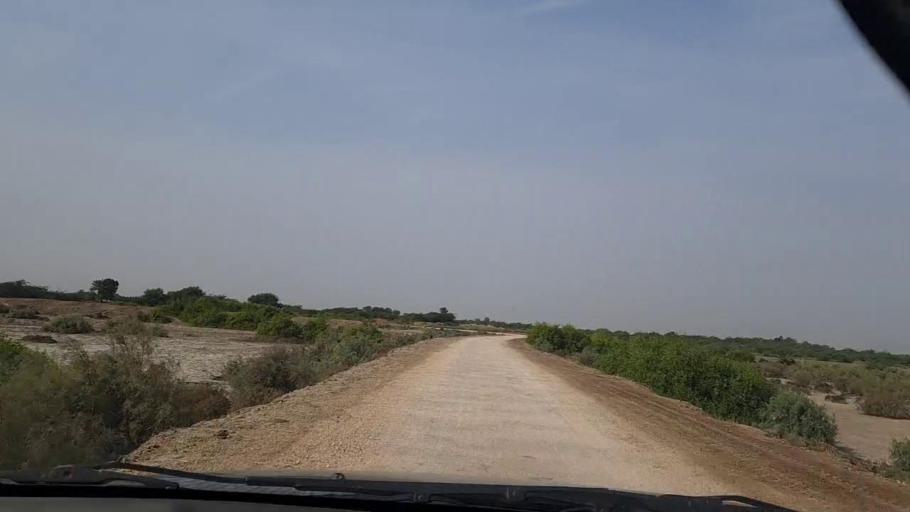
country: PK
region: Sindh
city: Thatta
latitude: 24.6091
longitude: 67.9543
